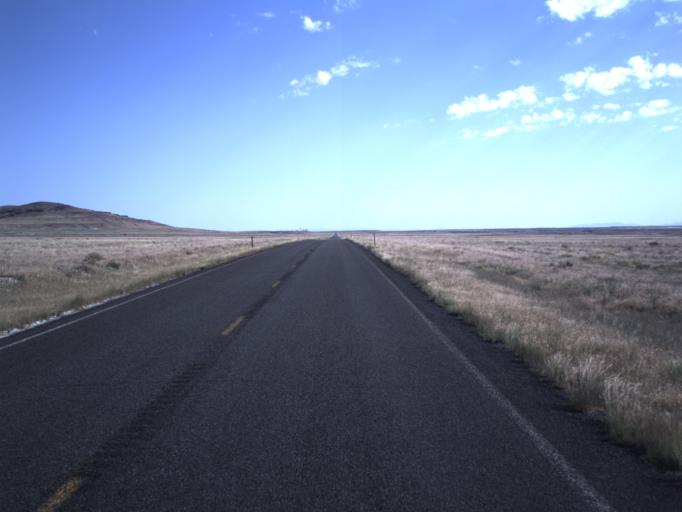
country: US
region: Utah
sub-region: Beaver County
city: Milford
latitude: 38.8484
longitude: -112.8430
